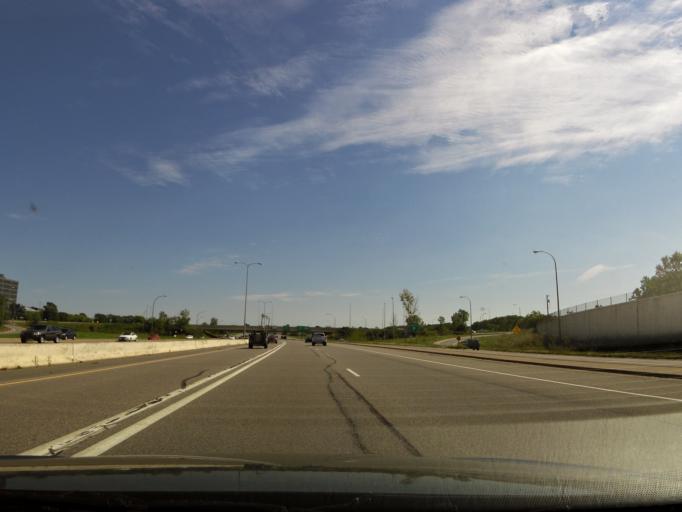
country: US
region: Minnesota
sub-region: Hennepin County
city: Minnetonka Mills
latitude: 44.9730
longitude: -93.4049
